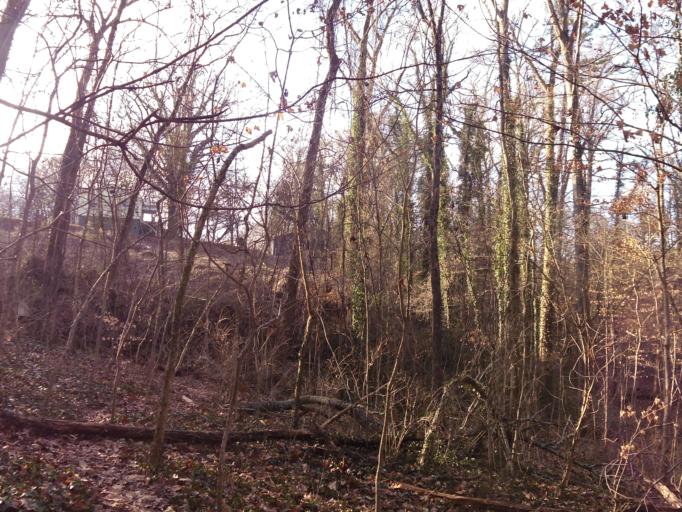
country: US
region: Tennessee
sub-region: Knox County
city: Knoxville
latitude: 35.9568
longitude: -83.8715
